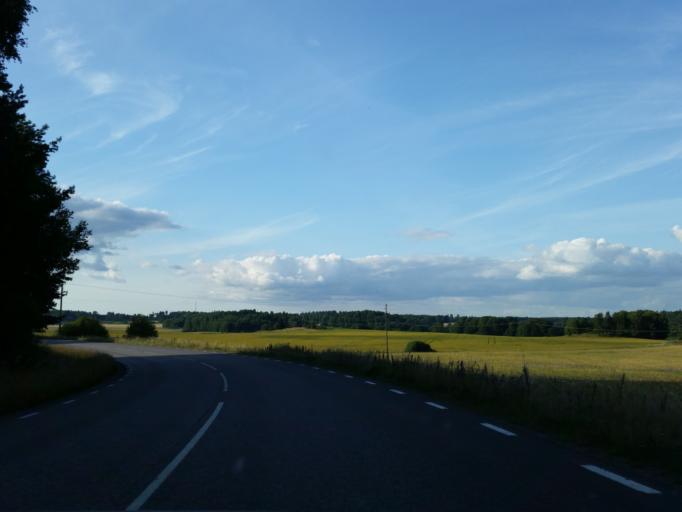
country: SE
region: Stockholm
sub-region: Sodertalje Kommun
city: Molnbo
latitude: 59.0107
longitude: 17.3763
